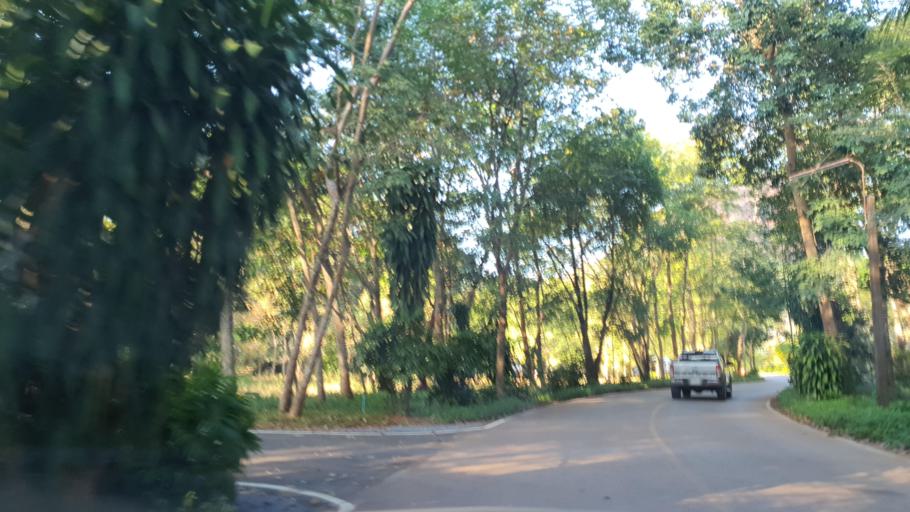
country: TH
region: Changwat Bueng Kan
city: Si Wilai
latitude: 18.1293
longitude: 103.8799
